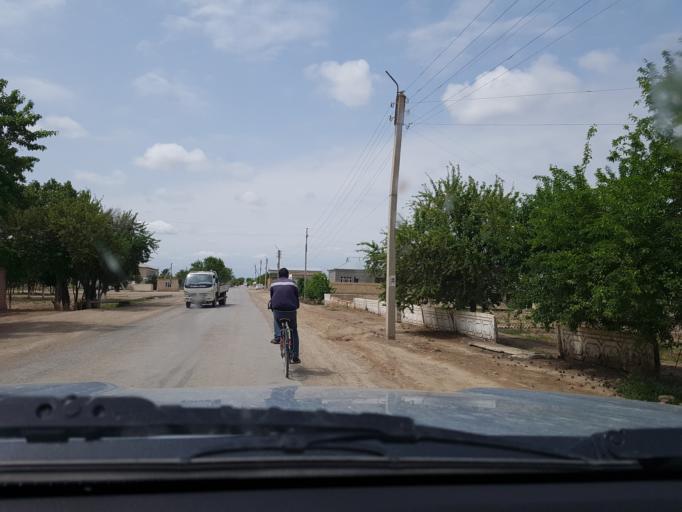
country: TM
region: Mary
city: Bayramaly
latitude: 37.6661
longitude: 62.1327
